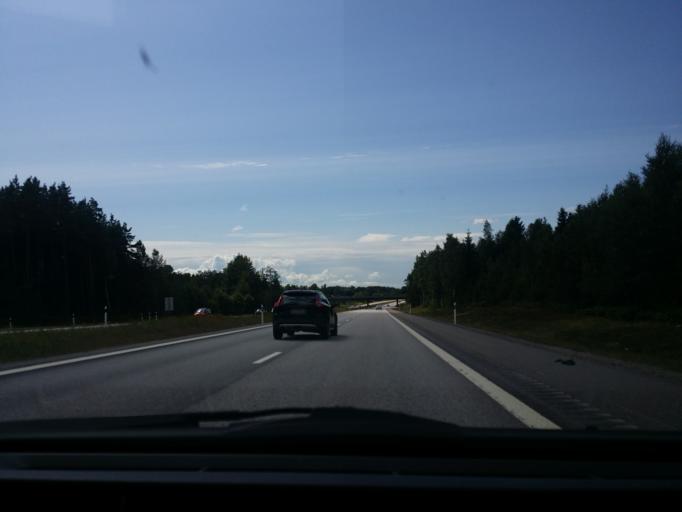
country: SE
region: OErebro
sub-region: Lindesbergs Kommun
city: Fellingsbro
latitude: 59.3388
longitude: 15.5389
